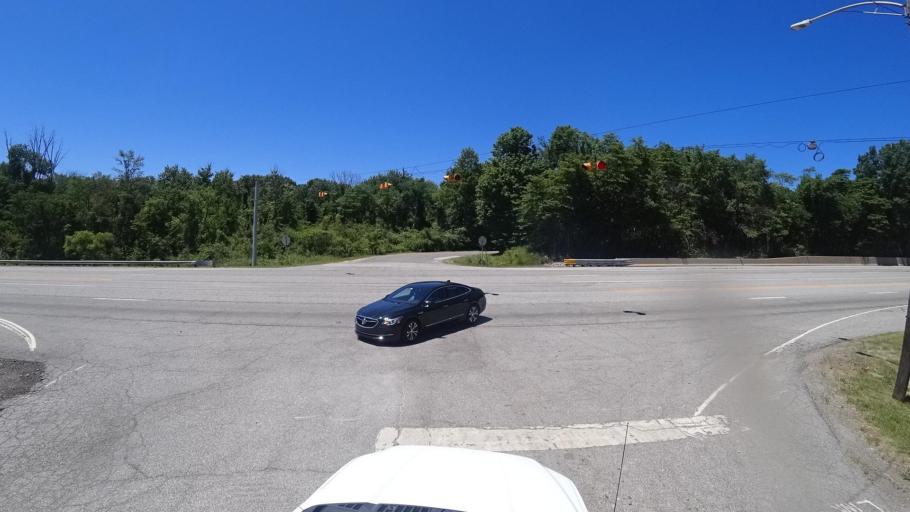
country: US
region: Indiana
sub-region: Porter County
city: Porter
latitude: 41.6232
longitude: -87.0862
